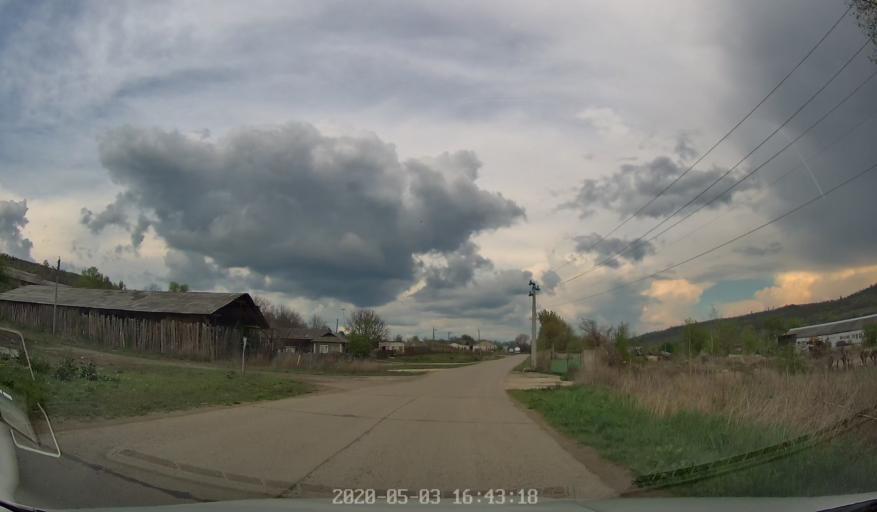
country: MD
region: Stinga Nistrului
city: Bucovat
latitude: 47.1624
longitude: 28.4271
